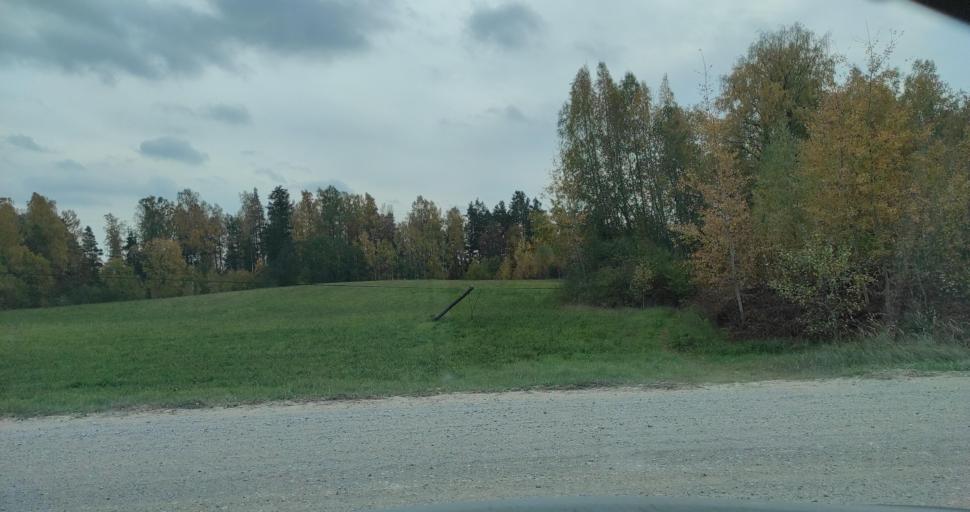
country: LV
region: Alsunga
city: Alsunga
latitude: 57.0332
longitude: 21.7037
